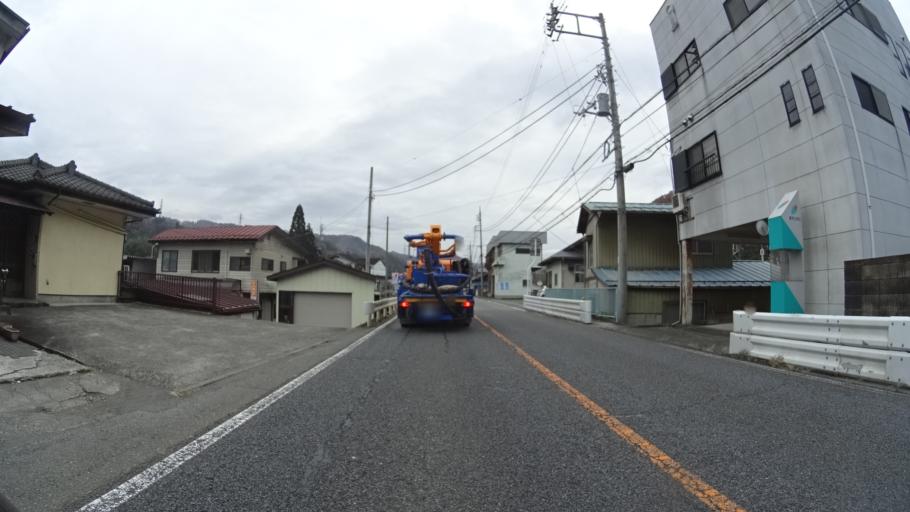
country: JP
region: Gunma
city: Numata
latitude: 36.6052
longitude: 139.0457
